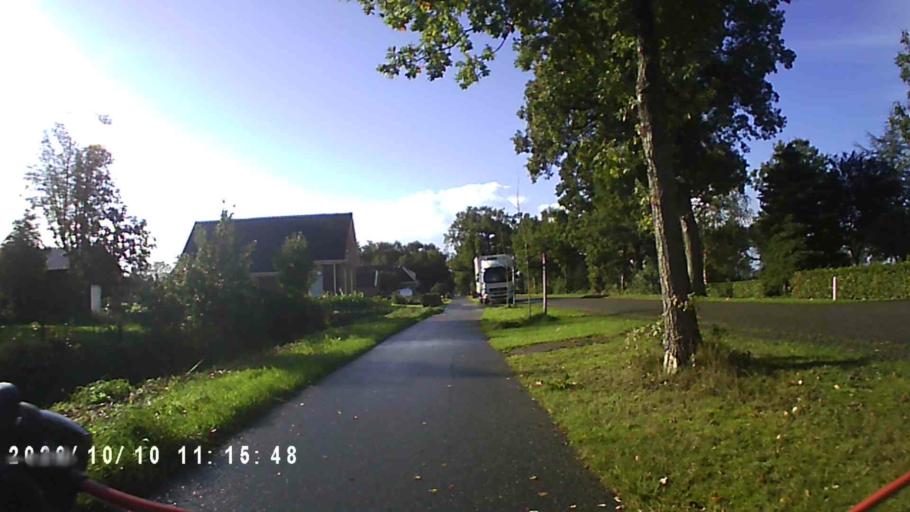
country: NL
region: Friesland
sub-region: Gemeente Smallingerland
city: Drachtstercompagnie
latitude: 53.1016
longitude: 6.2008
